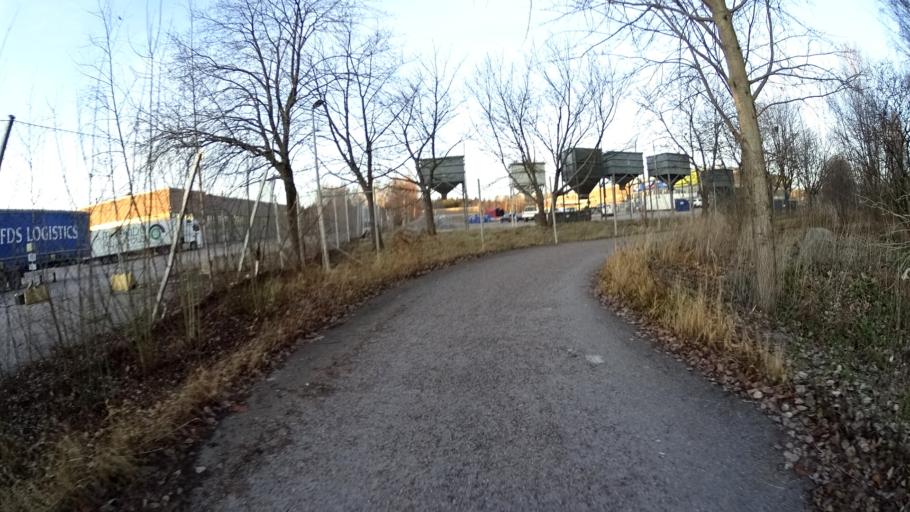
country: FI
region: Uusimaa
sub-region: Helsinki
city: Helsinki
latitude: 60.2101
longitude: 24.9212
